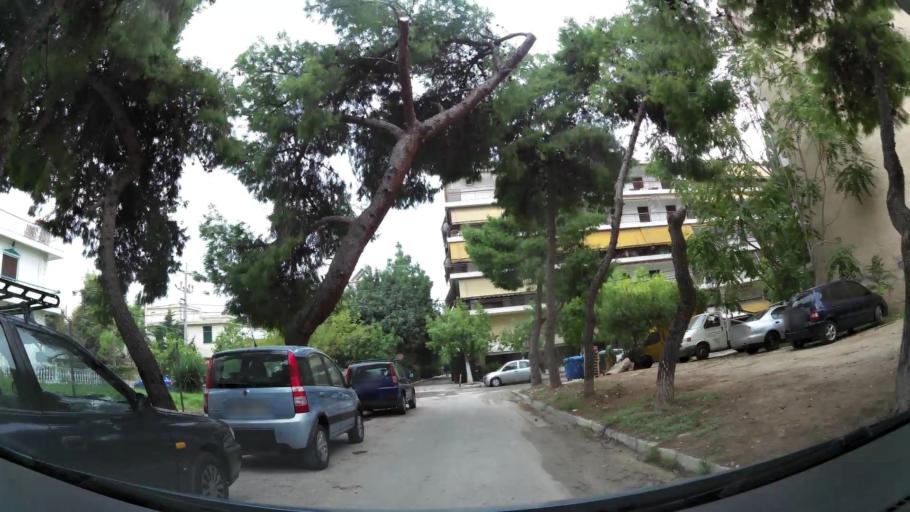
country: GR
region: Attica
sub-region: Nomarchia Athinas
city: Palaio Faliro
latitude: 37.9269
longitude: 23.7076
